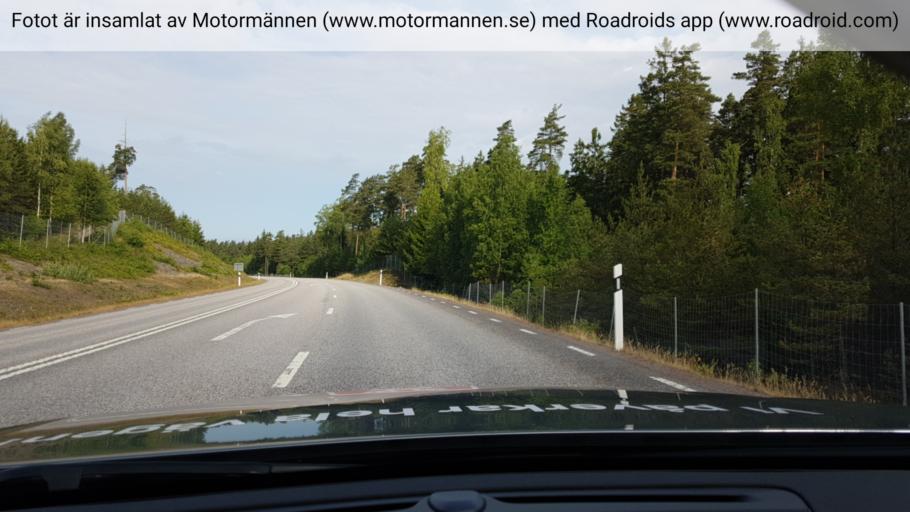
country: SE
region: OEstergoetland
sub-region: Motala Kommun
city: Borensberg
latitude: 58.5708
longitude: 15.2986
